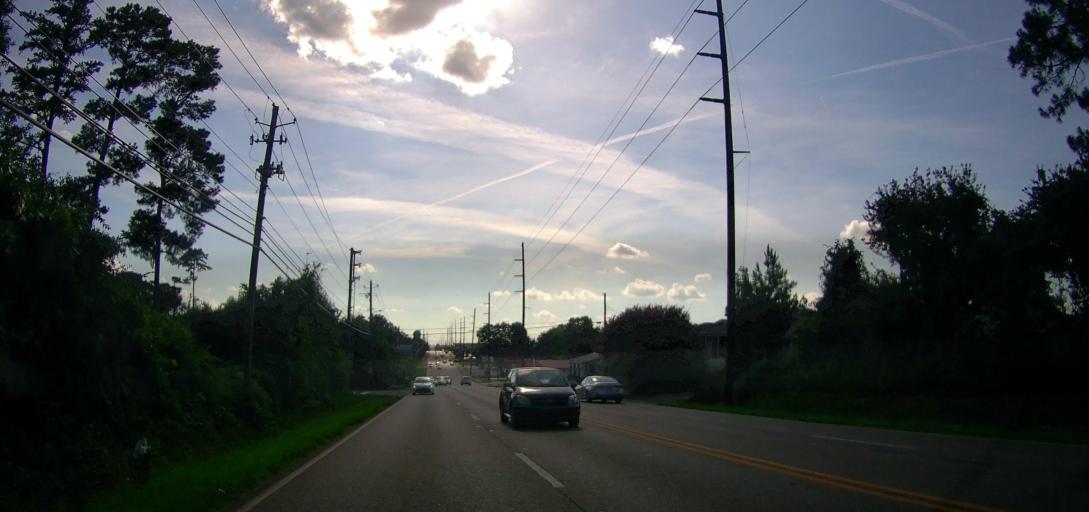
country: US
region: Alabama
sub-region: Tuscaloosa County
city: Holt
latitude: 33.2065
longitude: -87.4951
